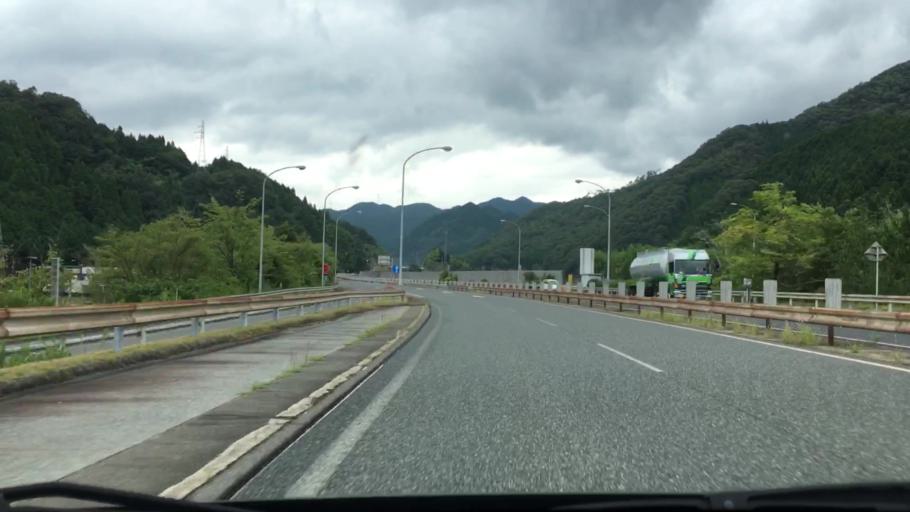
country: JP
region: Okayama
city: Niimi
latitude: 34.9985
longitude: 133.4465
